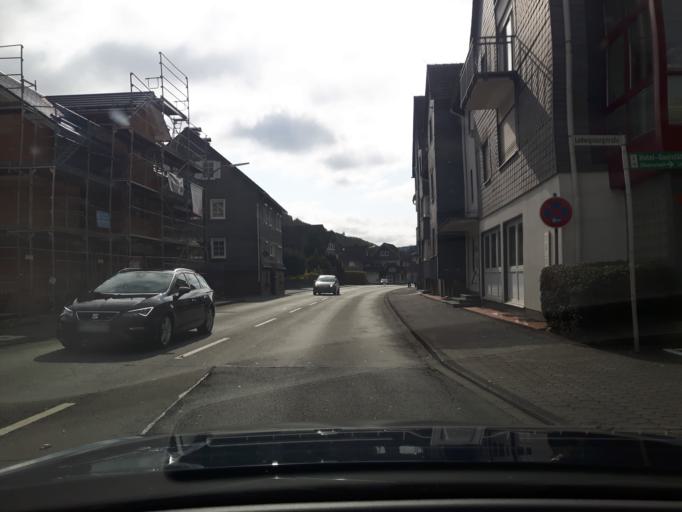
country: DE
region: North Rhine-Westphalia
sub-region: Regierungsbezirk Arnsberg
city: Bad Berleburg
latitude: 51.0476
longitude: 8.3921
